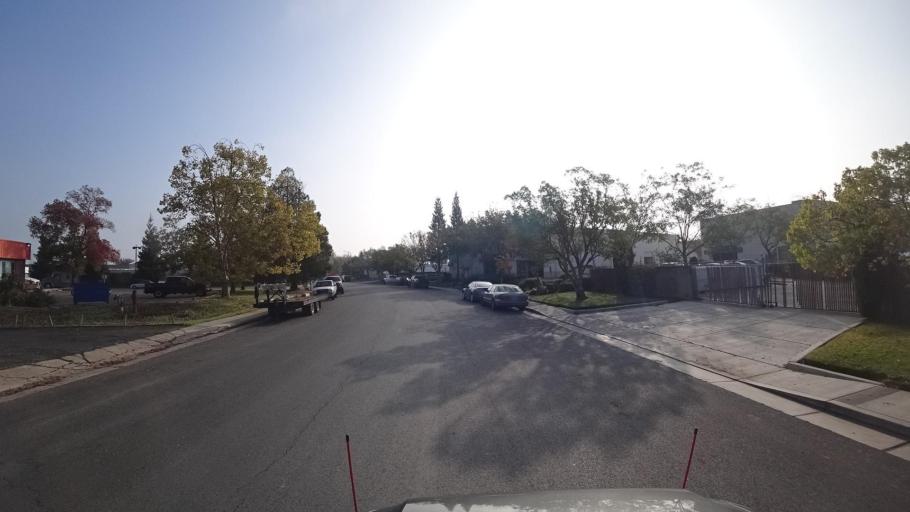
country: US
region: California
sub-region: Sacramento County
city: Elk Grove
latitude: 38.3982
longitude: -121.3575
